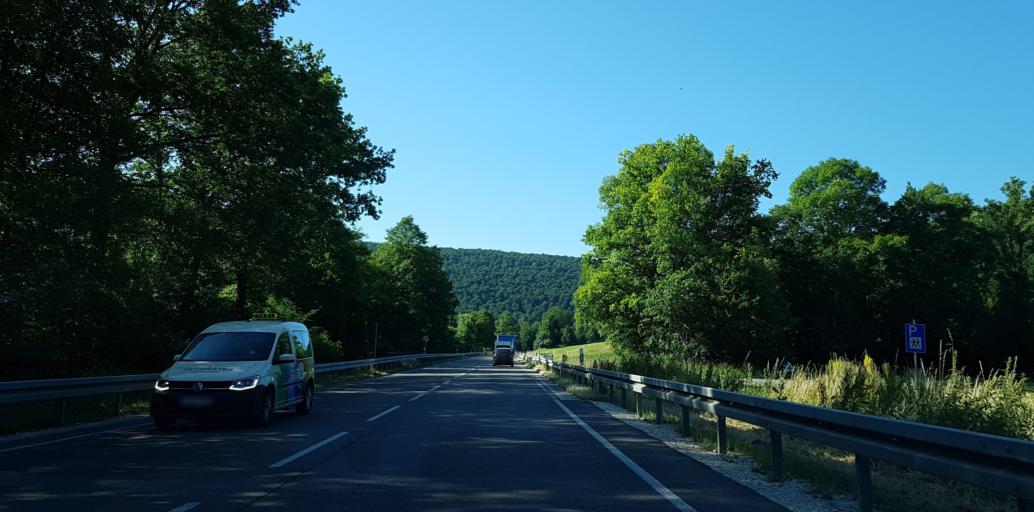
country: DE
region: Baden-Wuerttemberg
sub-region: Tuebingen Region
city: Blaubeuren
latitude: 48.3962
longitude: 9.7672
